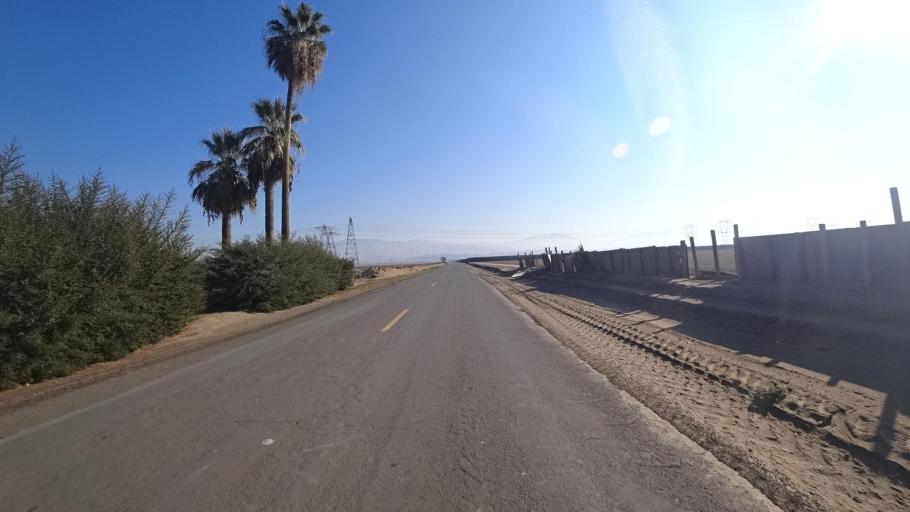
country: US
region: California
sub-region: Kern County
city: Arvin
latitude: 35.1217
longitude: -118.8992
